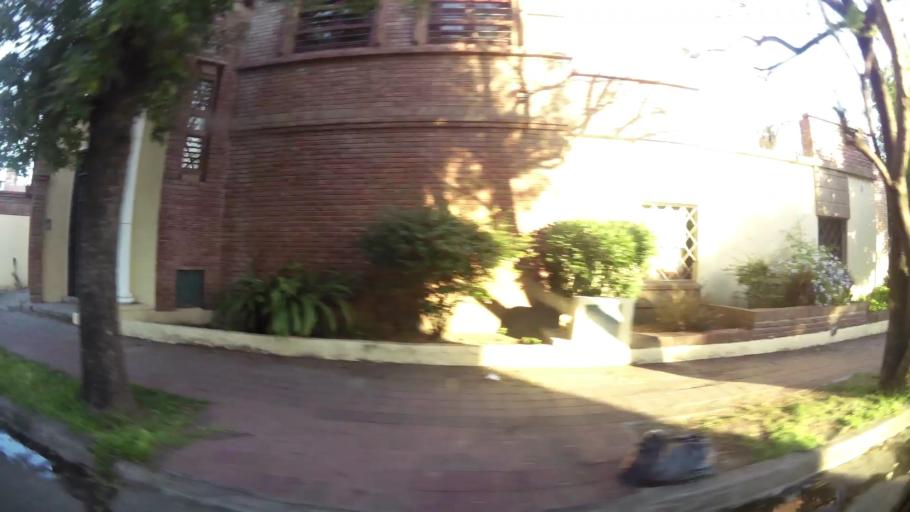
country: AR
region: Cordoba
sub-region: Departamento de Capital
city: Cordoba
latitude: -31.3840
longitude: -64.2167
